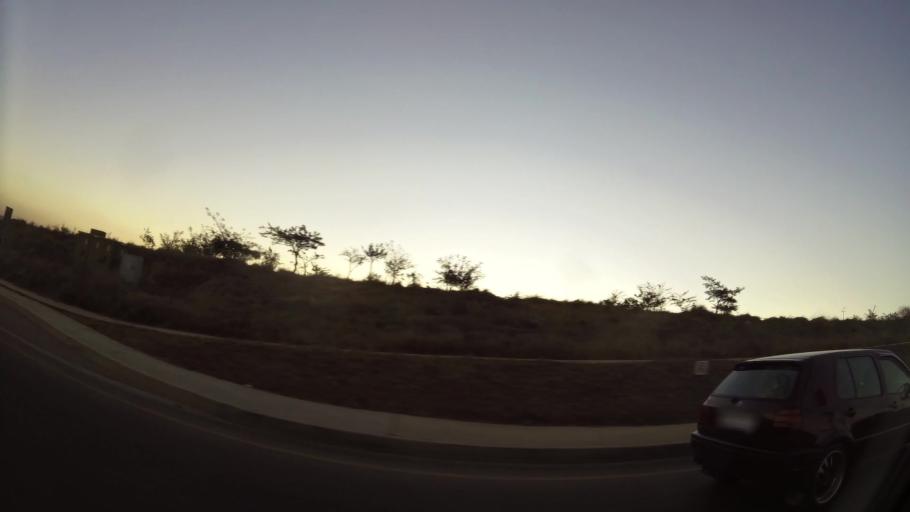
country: ZA
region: Gauteng
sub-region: City of Johannesburg Metropolitan Municipality
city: Diepsloot
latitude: -25.9743
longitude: 28.0204
